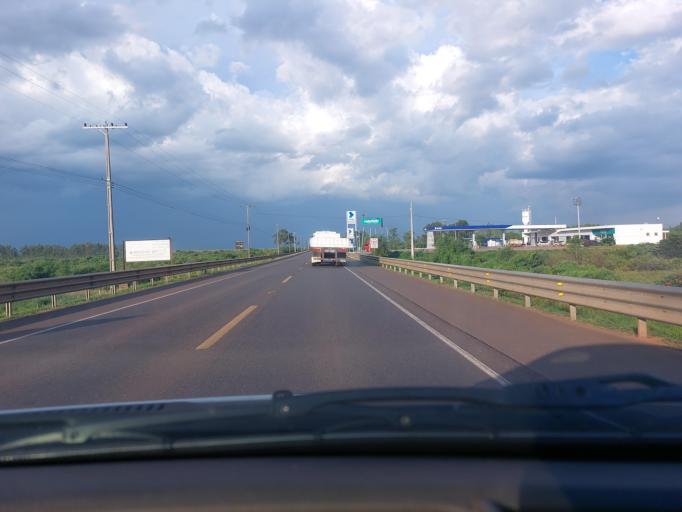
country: PY
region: Cordillera
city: Arroyos y Esteros
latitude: -25.0507
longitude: -57.0902
